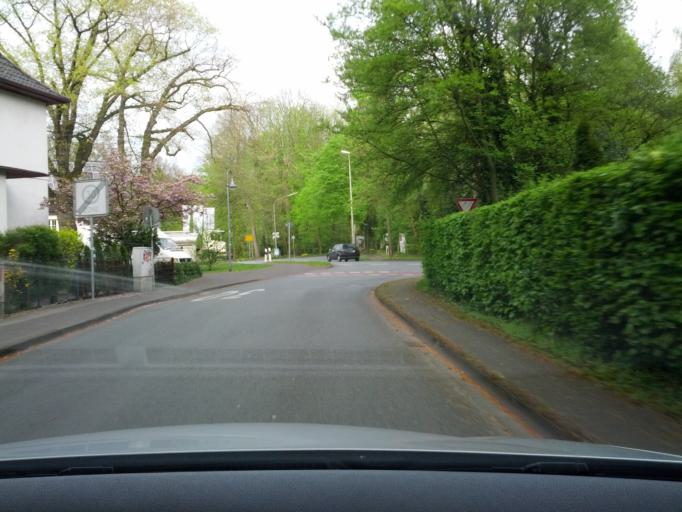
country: DE
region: North Rhine-Westphalia
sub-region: Regierungsbezirk Detmold
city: Guetersloh
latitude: 51.9443
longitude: 8.4118
